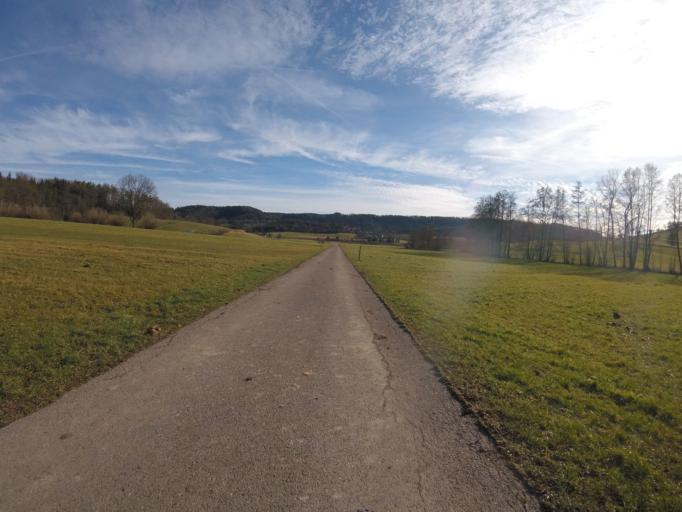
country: DE
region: Baden-Wuerttemberg
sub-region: Regierungsbezirk Stuttgart
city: Oberrot
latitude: 48.9860
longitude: 9.6573
